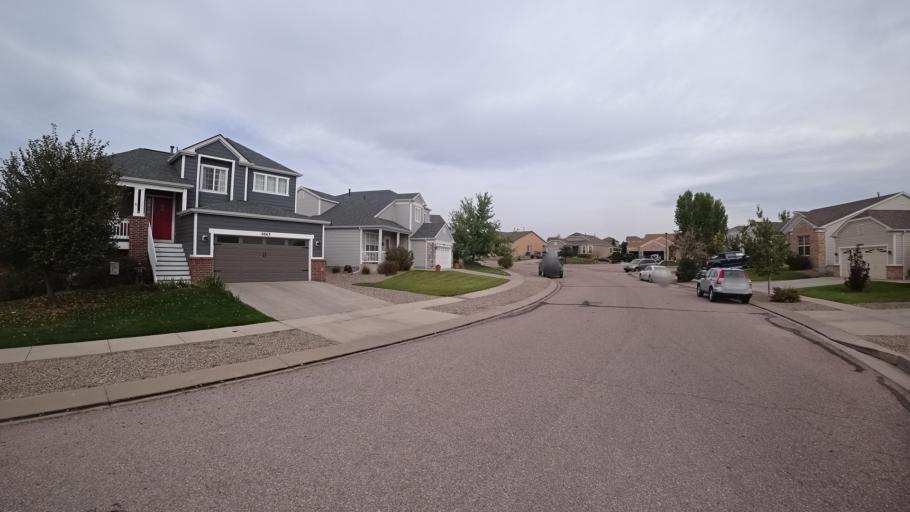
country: US
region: Colorado
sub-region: El Paso County
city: Cimarron Hills
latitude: 38.9249
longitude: -104.7001
